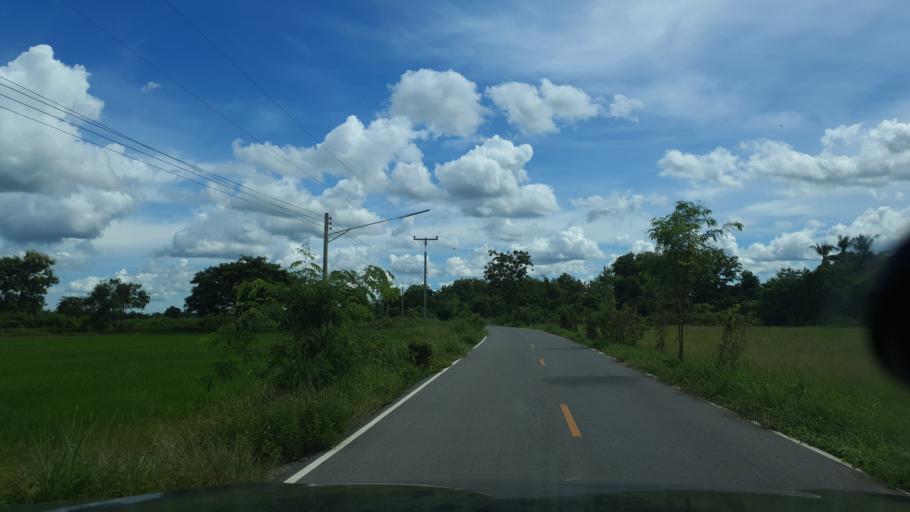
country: TH
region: Sukhothai
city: Thung Saliam
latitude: 17.3508
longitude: 99.6406
